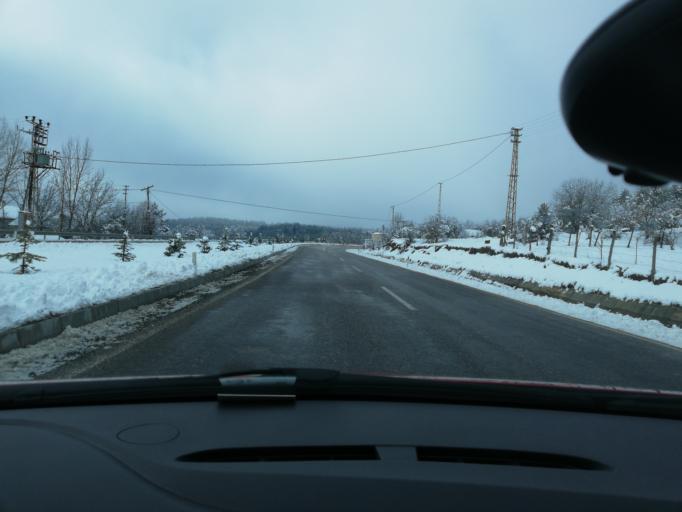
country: TR
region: Kastamonu
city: Ihsangazi
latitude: 41.3018
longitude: 33.5413
